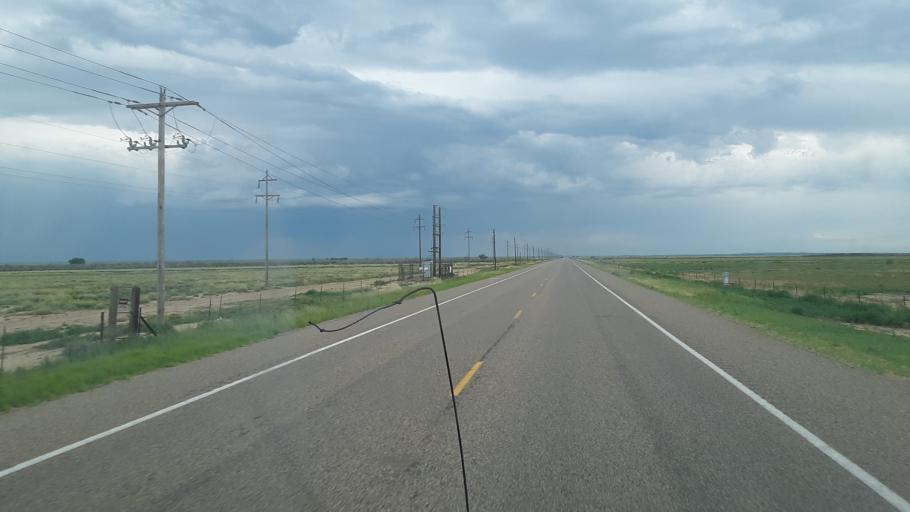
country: US
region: Colorado
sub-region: Crowley County
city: Ordway
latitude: 38.1887
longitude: -103.7481
